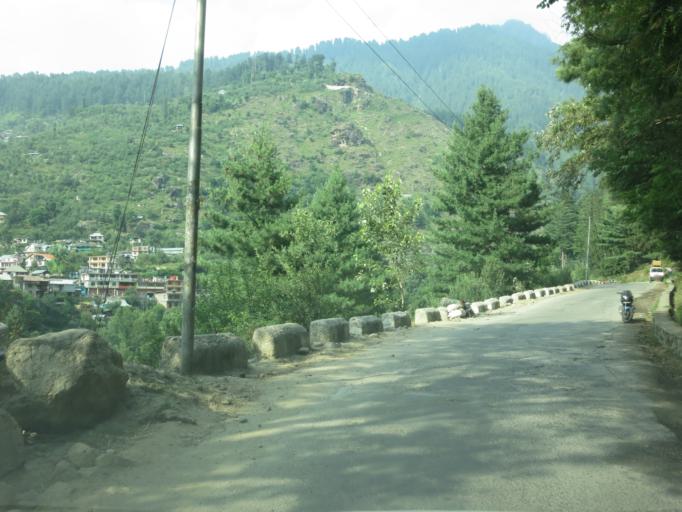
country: IN
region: Himachal Pradesh
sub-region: Kulu
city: Nagar
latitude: 32.1954
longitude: 77.2015
